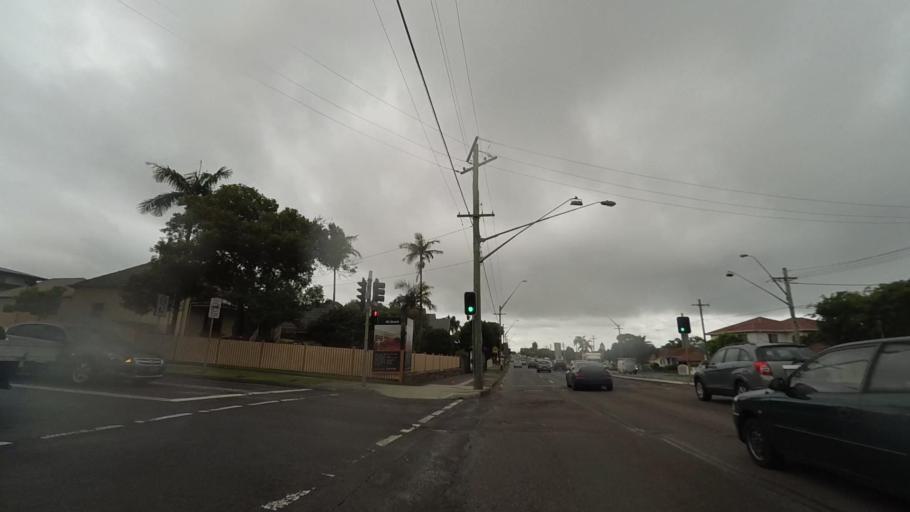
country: AU
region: New South Wales
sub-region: Rockdale
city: Dolls Point
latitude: -34.0012
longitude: 151.1265
